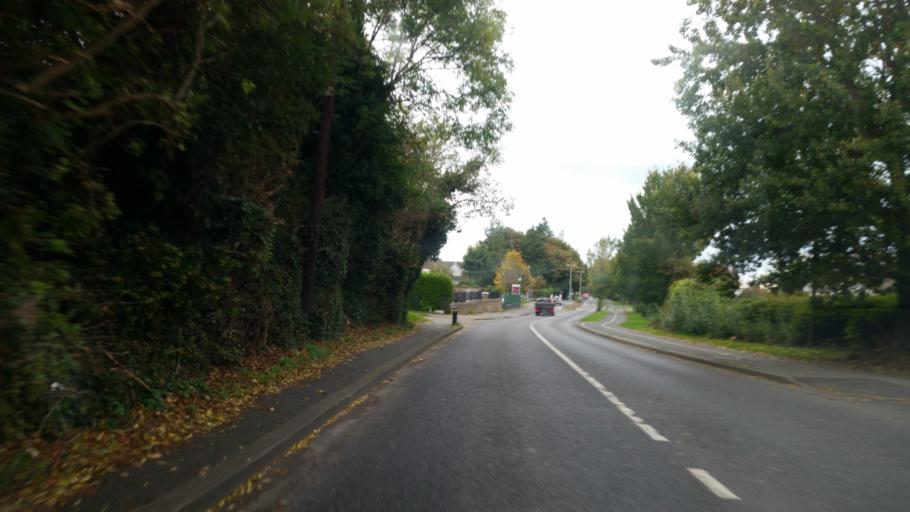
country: IE
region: Leinster
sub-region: Wicklow
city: Kilmacanoge
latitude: 53.1847
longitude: -6.1300
